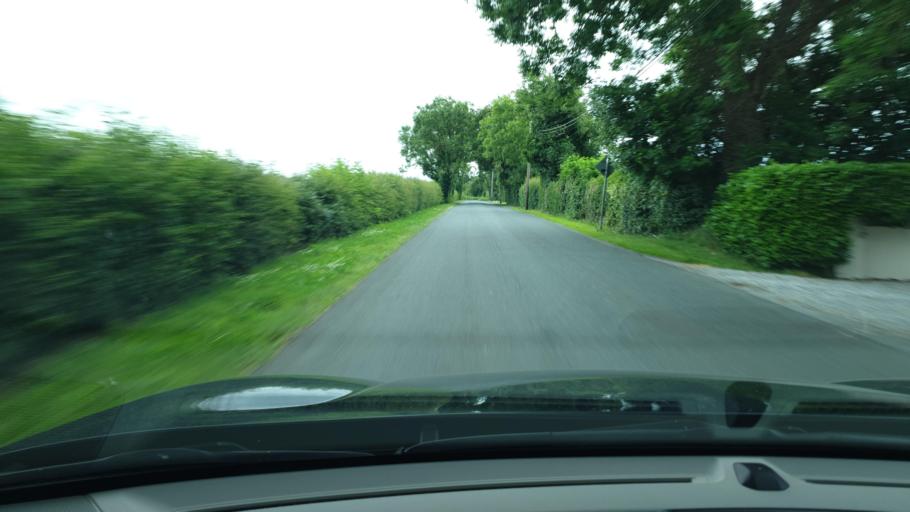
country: IE
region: Leinster
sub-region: An Mhi
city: Dunboyne
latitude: 53.4354
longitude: -6.4882
